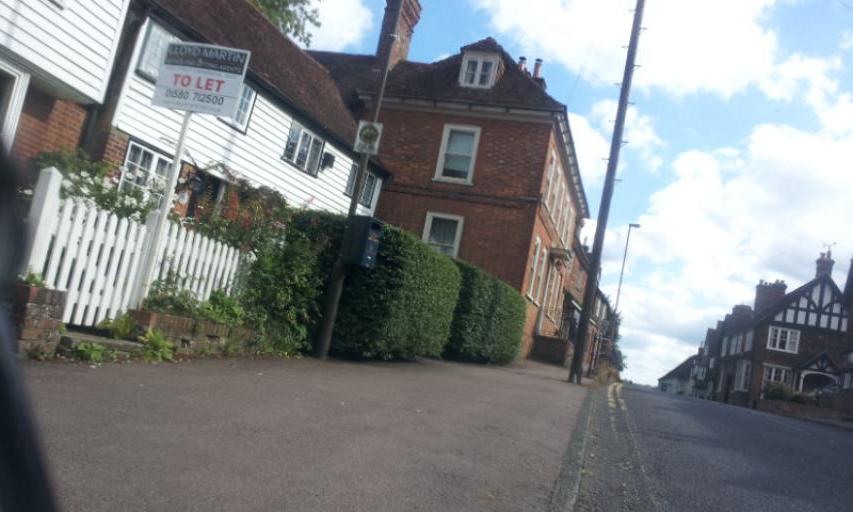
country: GB
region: England
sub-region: Kent
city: Staplehurst
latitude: 51.1588
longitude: 0.5525
